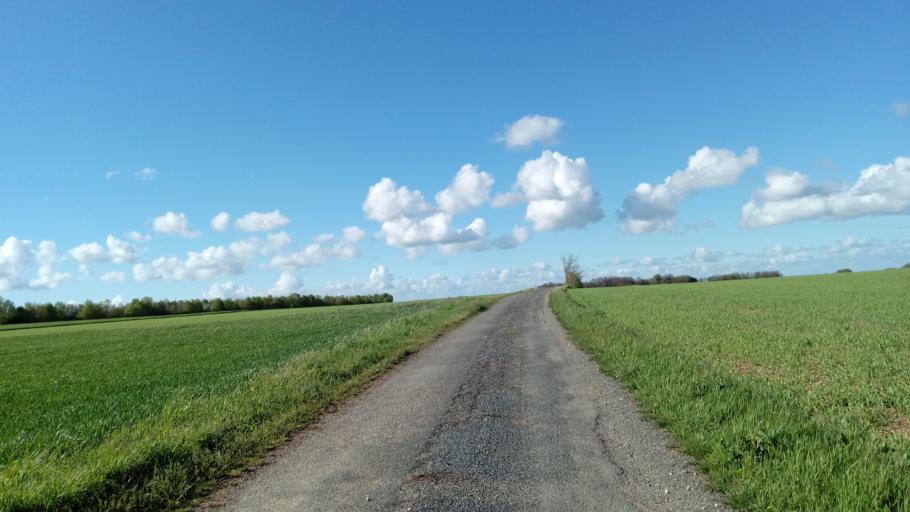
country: FR
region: Poitou-Charentes
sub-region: Departement de la Charente-Maritime
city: Verines
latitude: 46.1559
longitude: -0.9339
